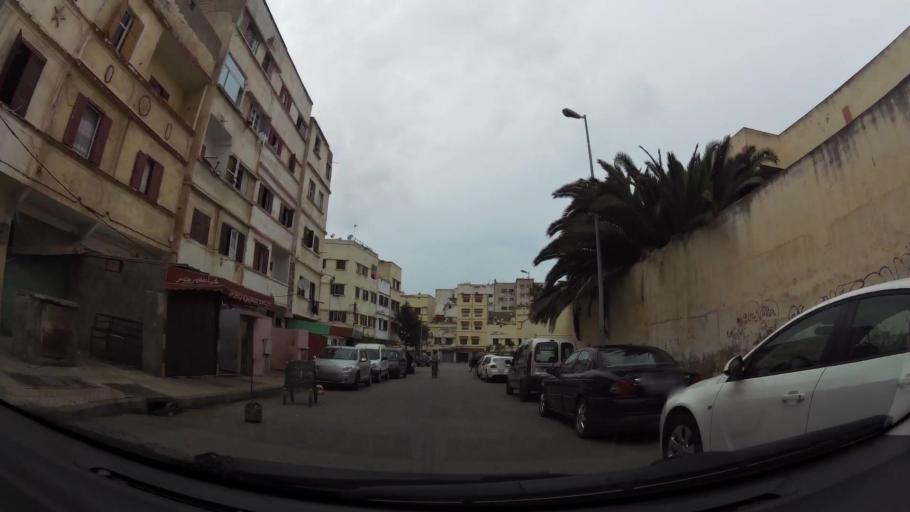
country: MA
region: Grand Casablanca
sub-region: Casablanca
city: Casablanca
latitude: 33.6024
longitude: -7.6376
